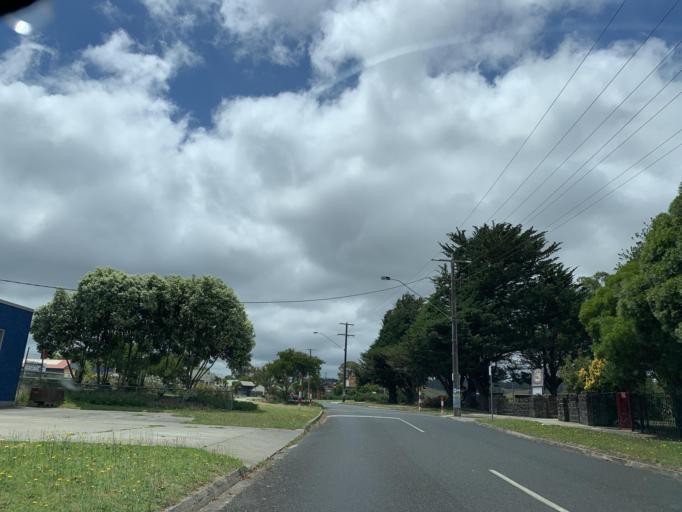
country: AU
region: Victoria
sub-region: Latrobe
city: Morwell
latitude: -38.1634
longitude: 146.3620
